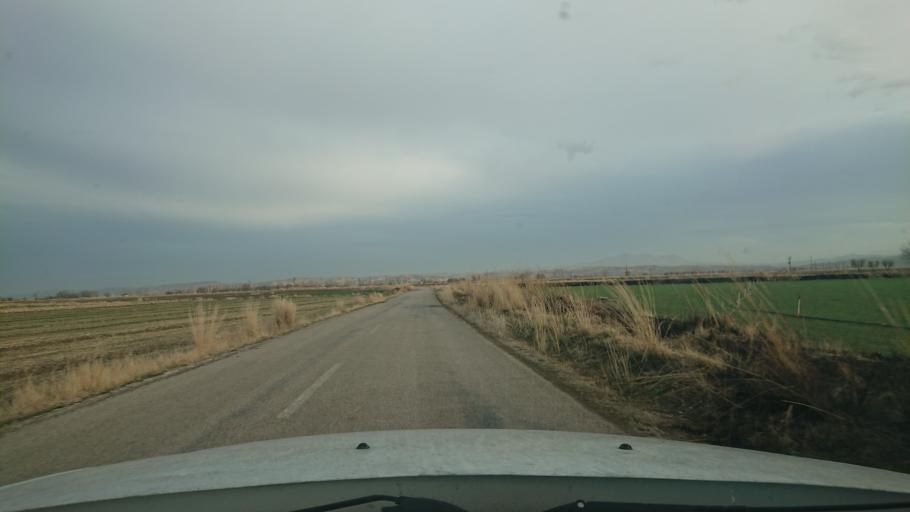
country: TR
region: Aksaray
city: Yesilova
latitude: 38.4335
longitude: 33.8370
